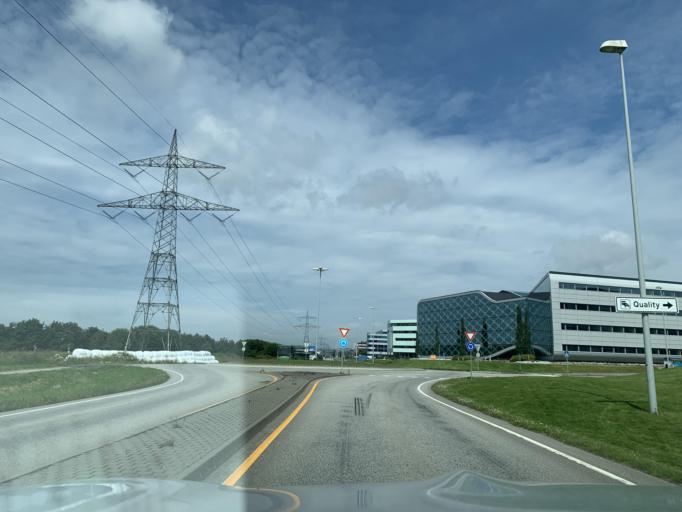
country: NO
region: Rogaland
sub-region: Sola
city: Sola
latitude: 58.8863
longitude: 5.6958
